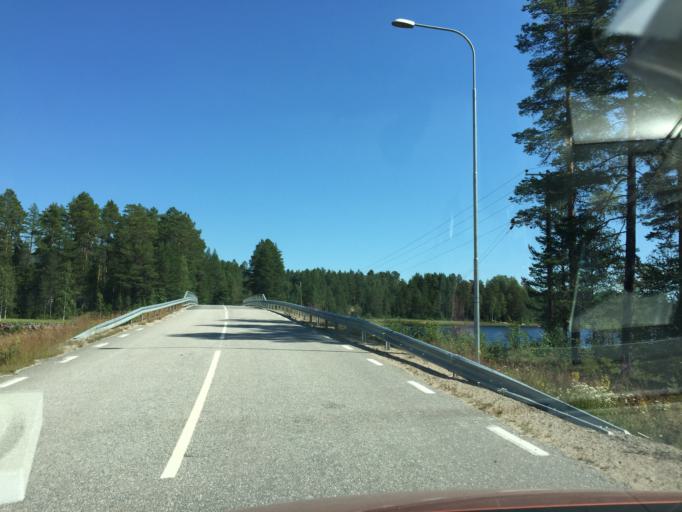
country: SE
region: Jaemtland
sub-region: Harjedalens Kommun
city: Sveg
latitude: 61.7796
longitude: 14.8659
